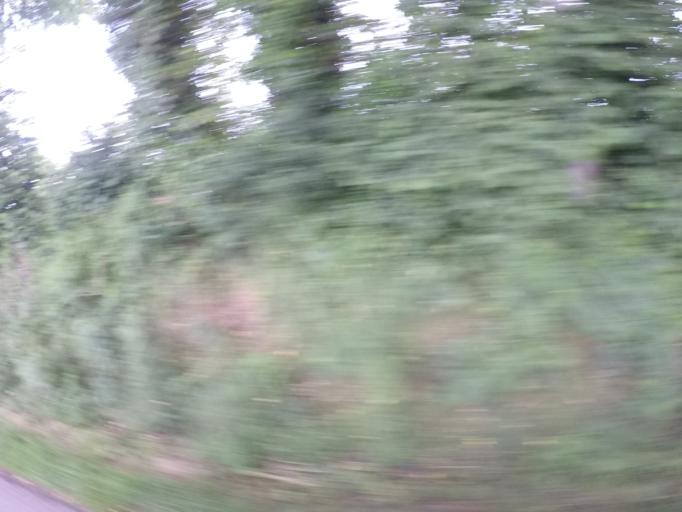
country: FR
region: Brittany
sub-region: Departement des Cotes-d'Armor
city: Goudelin
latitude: 48.6281
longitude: -3.0451
